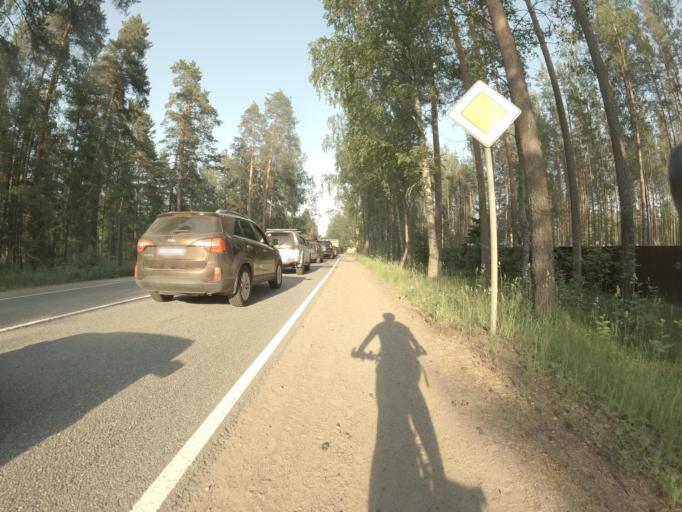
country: RU
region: Leningrad
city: Veshchevo
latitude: 60.4715
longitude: 29.2712
